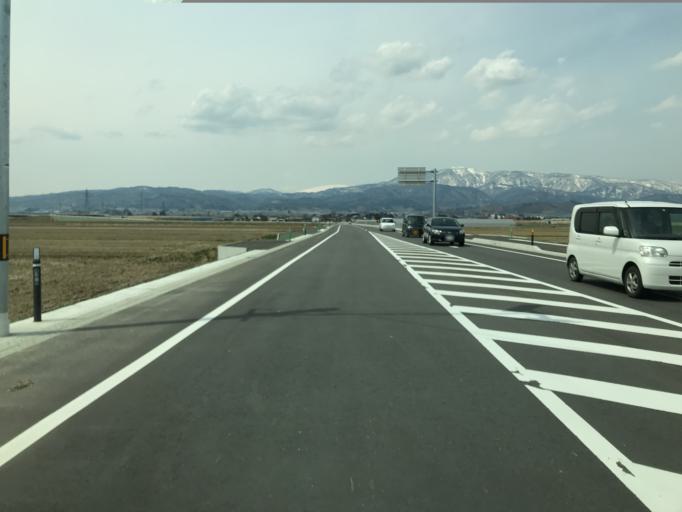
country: JP
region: Yamagata
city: Higashine
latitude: 38.4519
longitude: 140.3655
